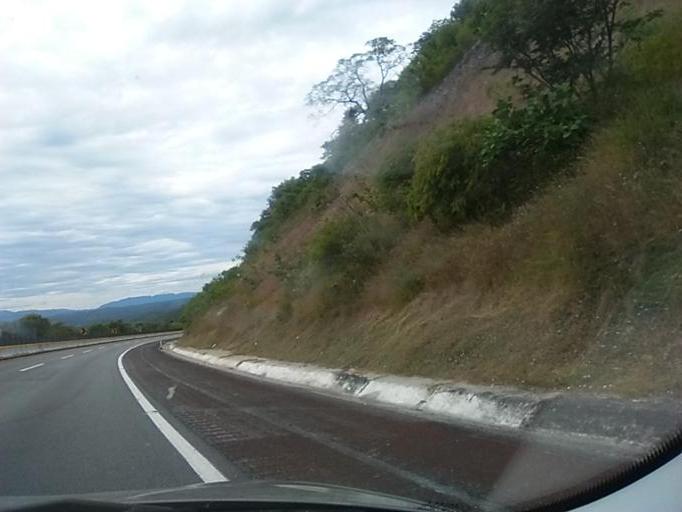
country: MX
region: Guerrero
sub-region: Huitzuco de los Figueroa
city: Ciudad de Huitzuco
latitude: 18.1859
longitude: -99.2037
